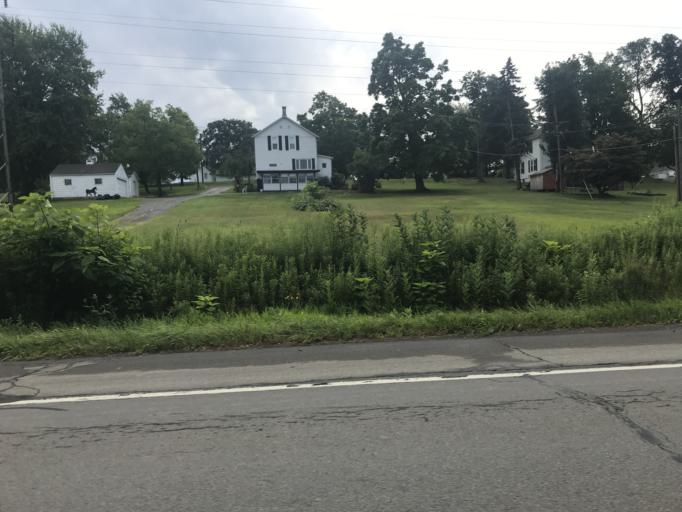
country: US
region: New York
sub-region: Chautauqua County
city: Silver Creek
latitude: 42.5502
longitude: -79.1635
